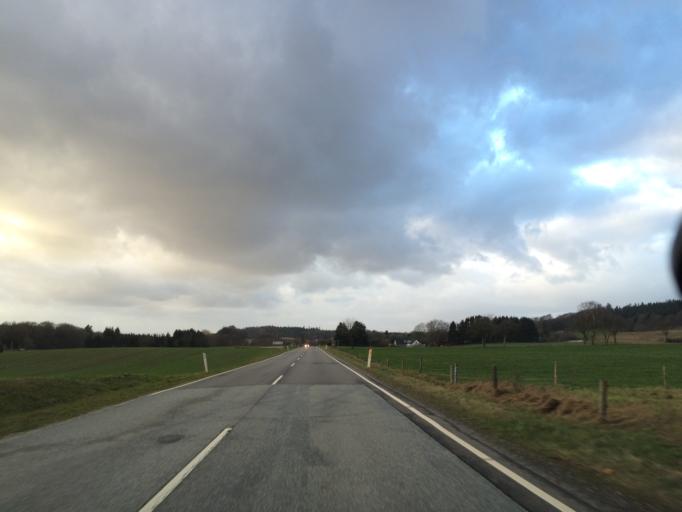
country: DK
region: Central Jutland
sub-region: Silkeborg Kommune
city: Svejbaek
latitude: 56.0917
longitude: 9.6702
